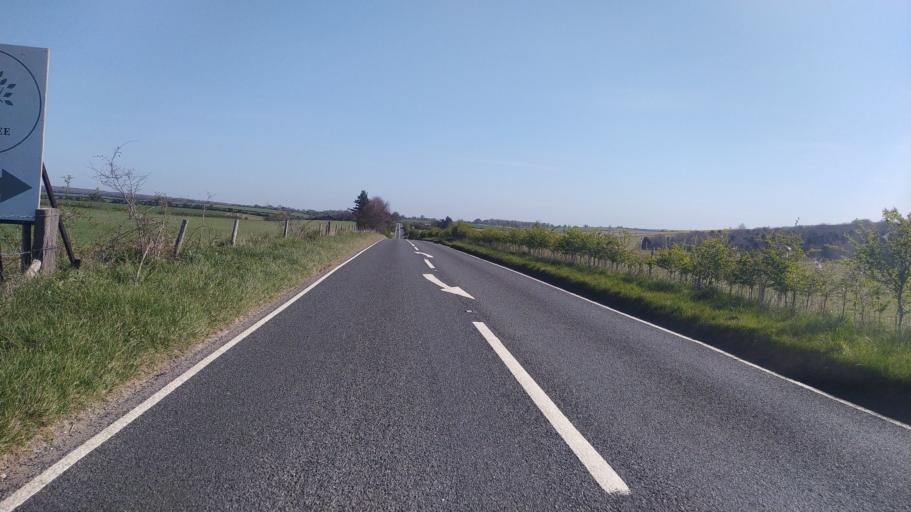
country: GB
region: England
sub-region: Wiltshire
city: Bower Chalke
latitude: 50.9541
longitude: -1.9779
